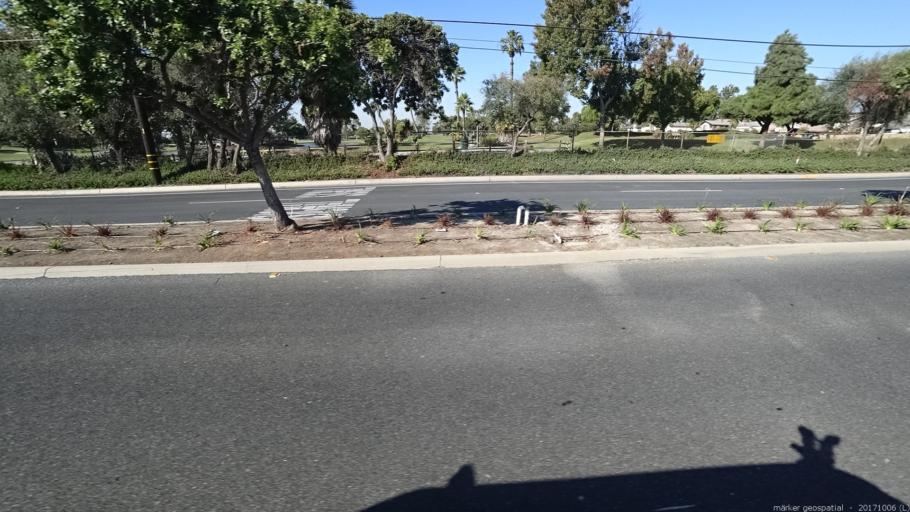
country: US
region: California
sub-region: Orange County
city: Los Alamitos
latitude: 33.7811
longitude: -118.0459
